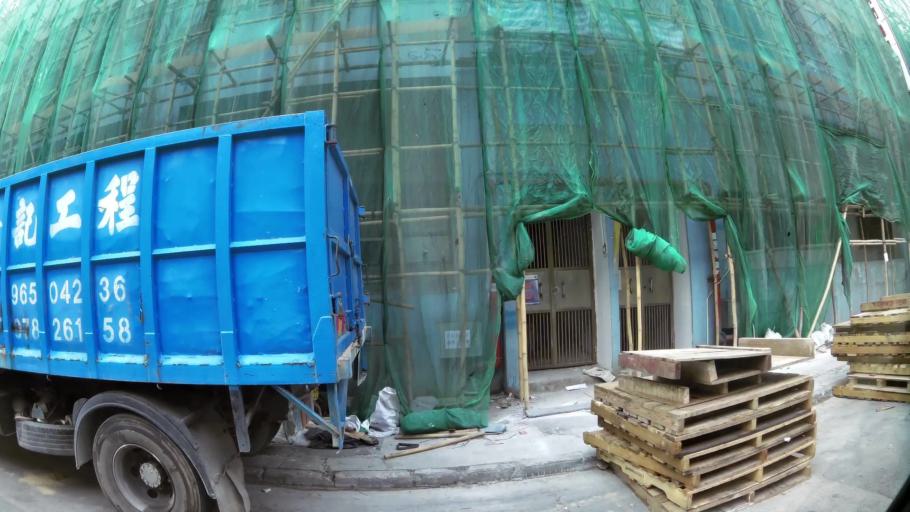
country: HK
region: Kowloon City
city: Kowloon
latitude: 22.2937
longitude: 114.2345
